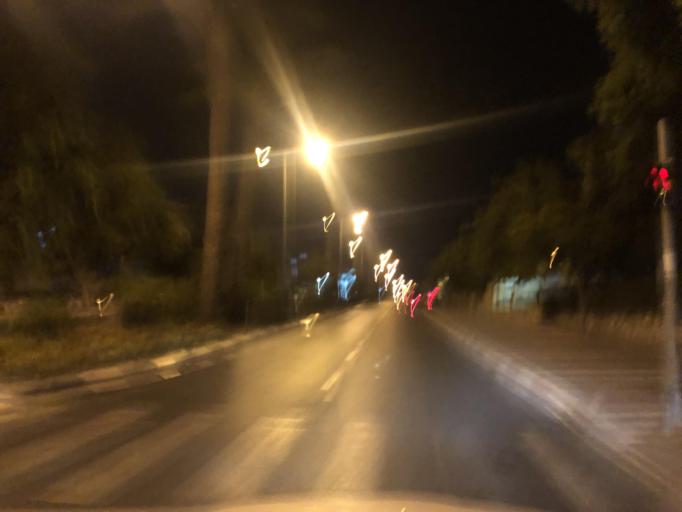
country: IL
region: Tel Aviv
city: Azor
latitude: 32.0465
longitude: 34.8011
